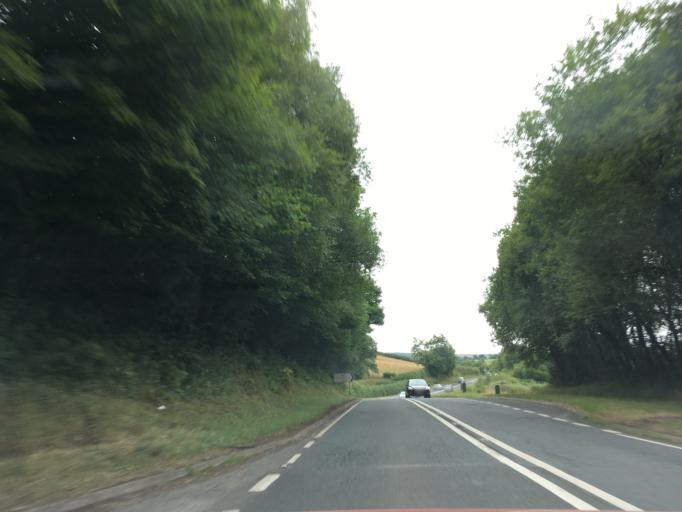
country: GB
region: Wales
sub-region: Sir Powys
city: Cray
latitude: 51.9526
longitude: -3.5343
